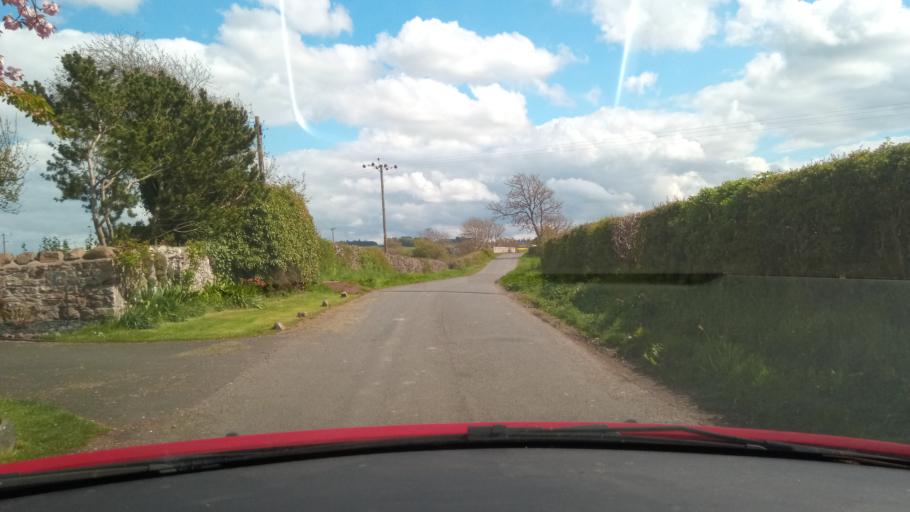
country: GB
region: Scotland
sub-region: The Scottish Borders
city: Saint Boswells
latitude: 55.5618
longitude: -2.6179
